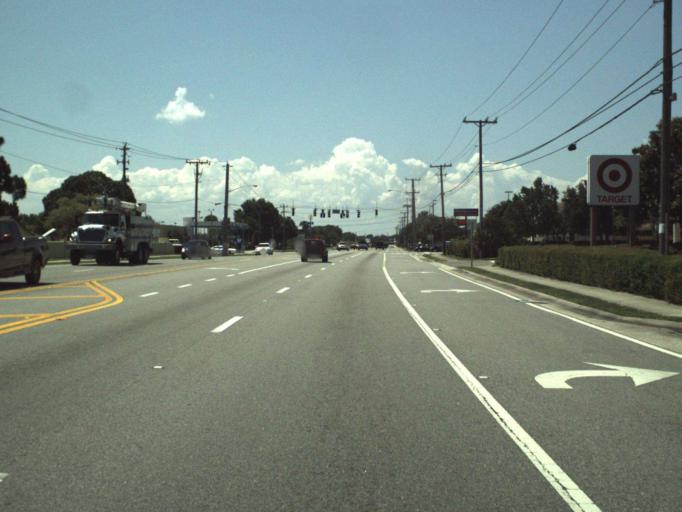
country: US
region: Florida
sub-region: Brevard County
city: Cocoa
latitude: 28.3866
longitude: -80.7030
